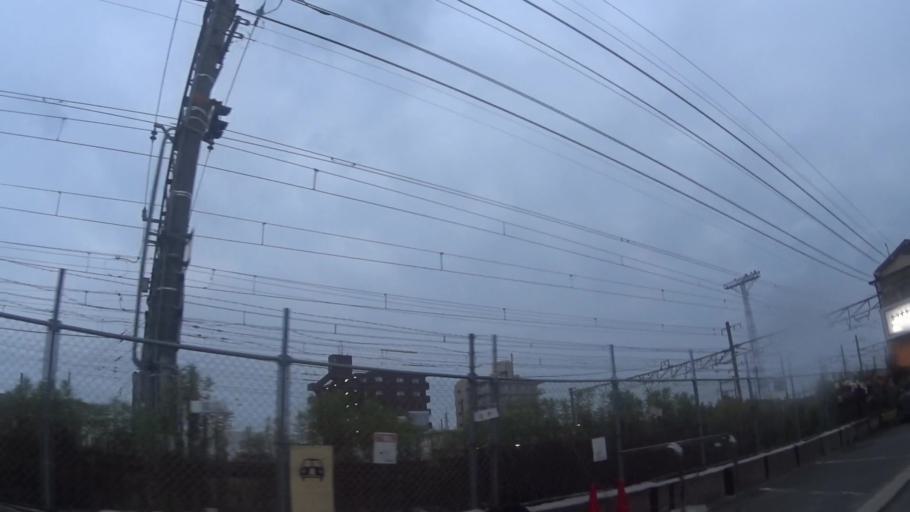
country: JP
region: Kyoto
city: Muko
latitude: 34.9517
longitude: 135.7094
